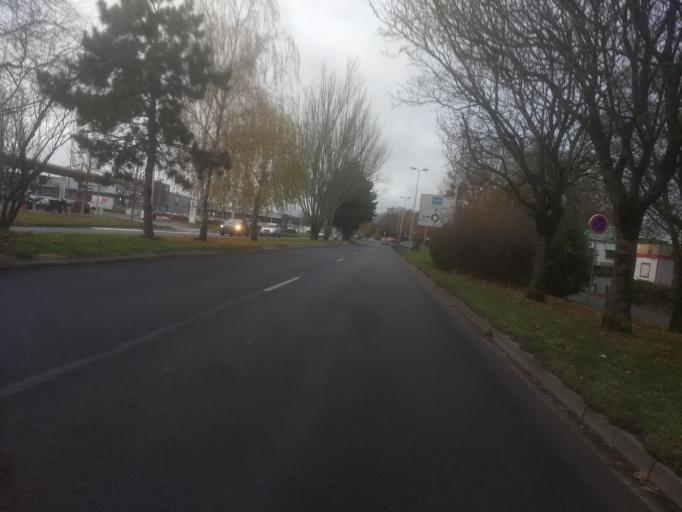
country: FR
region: Nord-Pas-de-Calais
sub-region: Departement du Pas-de-Calais
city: Anzin-Saint-Aubin
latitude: 50.3007
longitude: 2.7365
